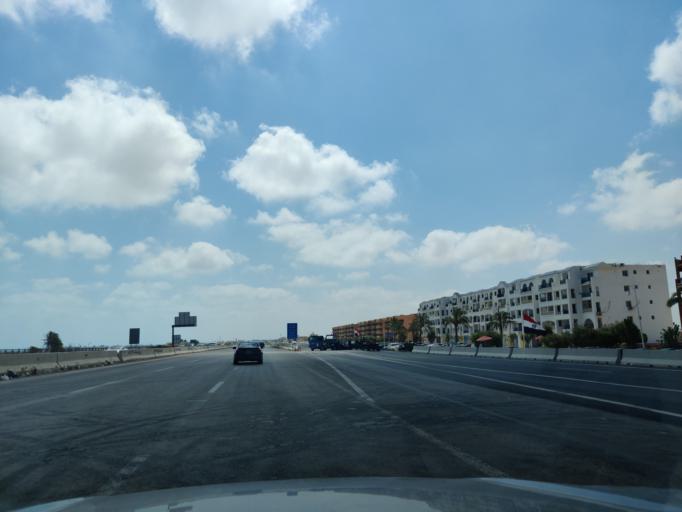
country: EG
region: Muhafazat Matruh
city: Al `Alamayn
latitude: 30.8221
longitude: 28.9989
